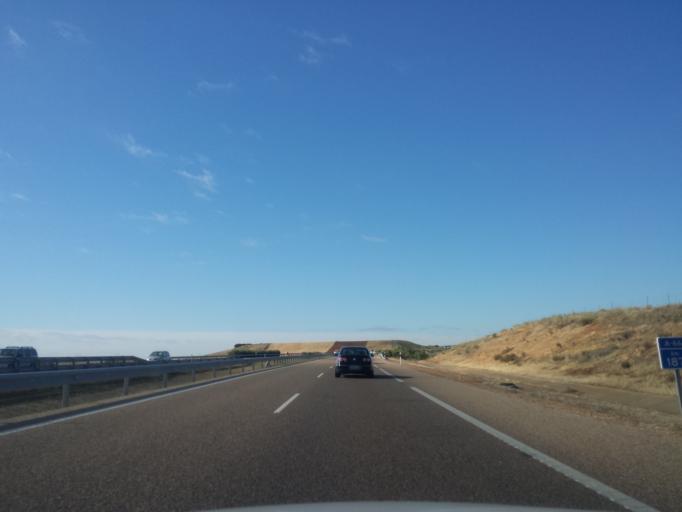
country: ES
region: Castille and Leon
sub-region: Provincia de Leon
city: Algadefe
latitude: 42.2057
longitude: -5.6002
